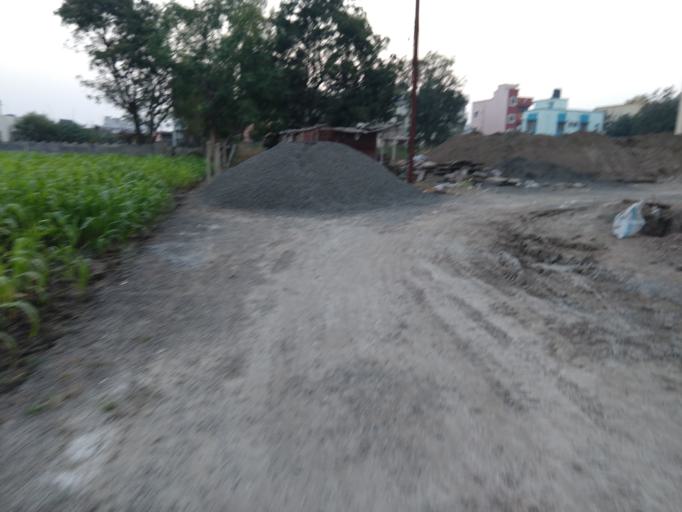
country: IN
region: Maharashtra
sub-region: Pune Division
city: Pune
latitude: 18.4385
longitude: 73.9136
